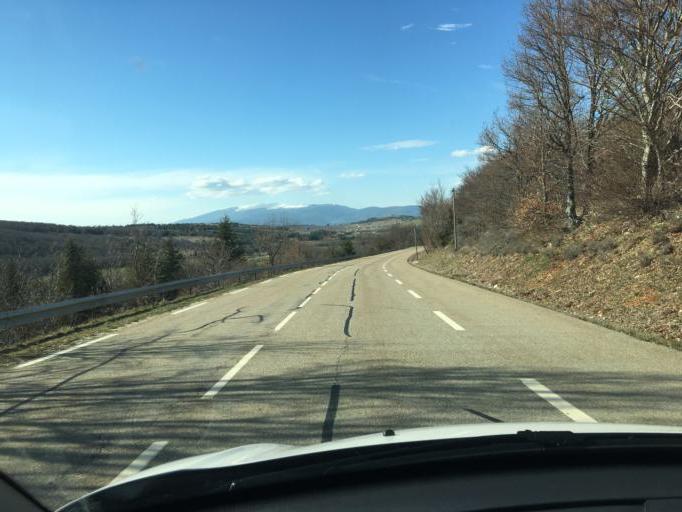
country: FR
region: Provence-Alpes-Cote d'Azur
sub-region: Departement du Vaucluse
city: Sault
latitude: 44.0077
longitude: 5.4775
